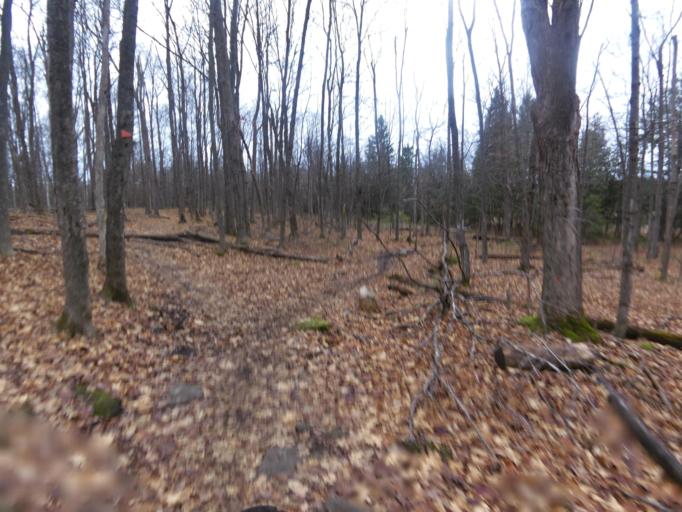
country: CA
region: Ontario
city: Bells Corners
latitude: 45.3087
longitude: -75.8429
